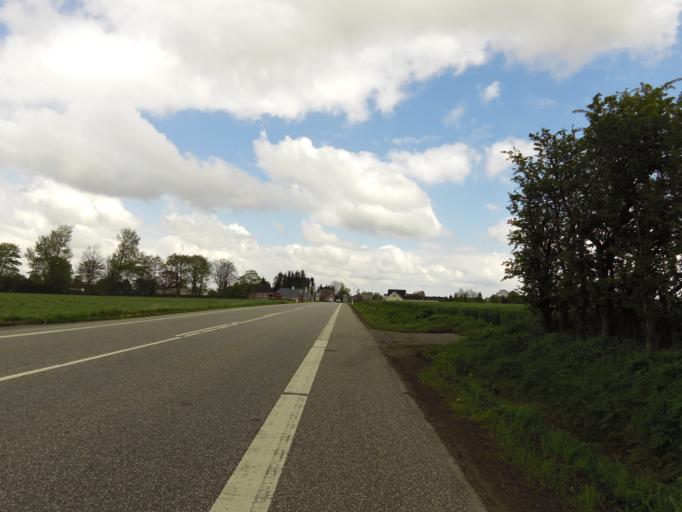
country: DK
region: South Denmark
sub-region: Haderslev Kommune
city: Gram
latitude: 55.2832
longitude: 9.0359
